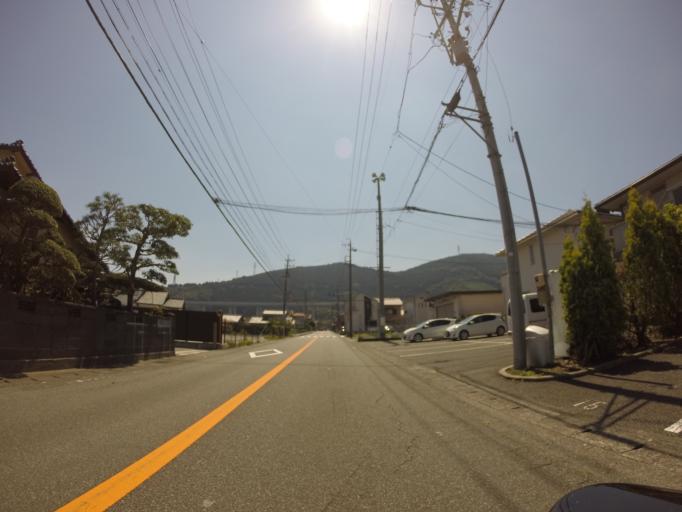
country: JP
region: Shizuoka
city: Fujinomiya
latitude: 35.1802
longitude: 138.6012
